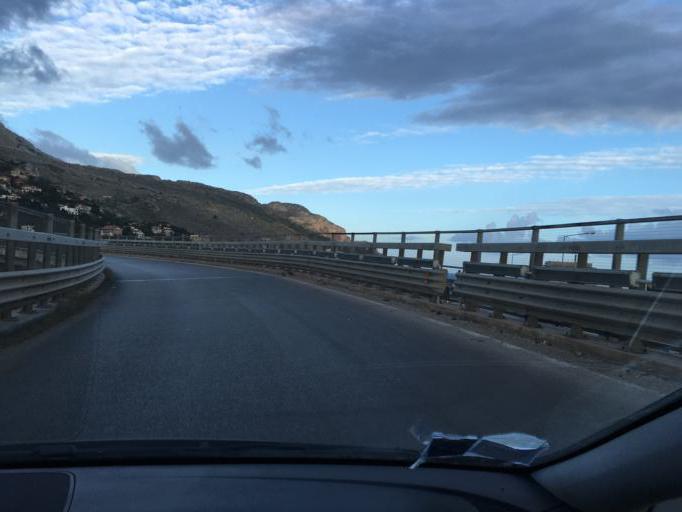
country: IT
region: Sicily
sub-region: Palermo
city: Isola delle Femmine
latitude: 38.1926
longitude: 13.2878
